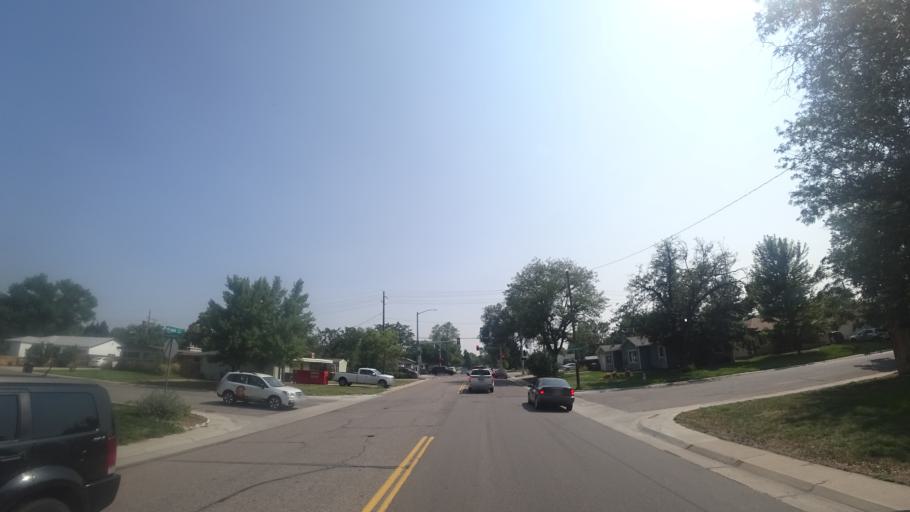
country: US
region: Colorado
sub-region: Arapahoe County
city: Englewood
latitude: 39.6248
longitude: -104.9833
